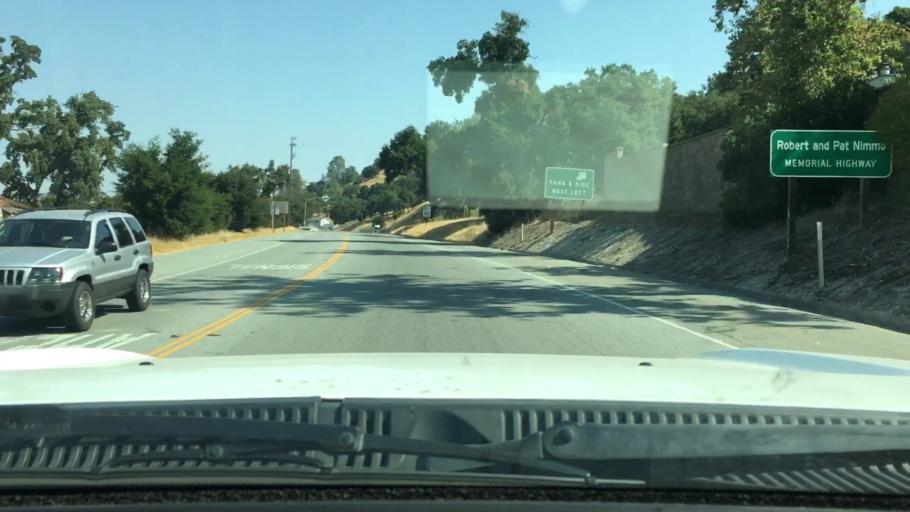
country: US
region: California
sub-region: San Luis Obispo County
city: Atascadero
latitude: 35.4889
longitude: -120.6630
